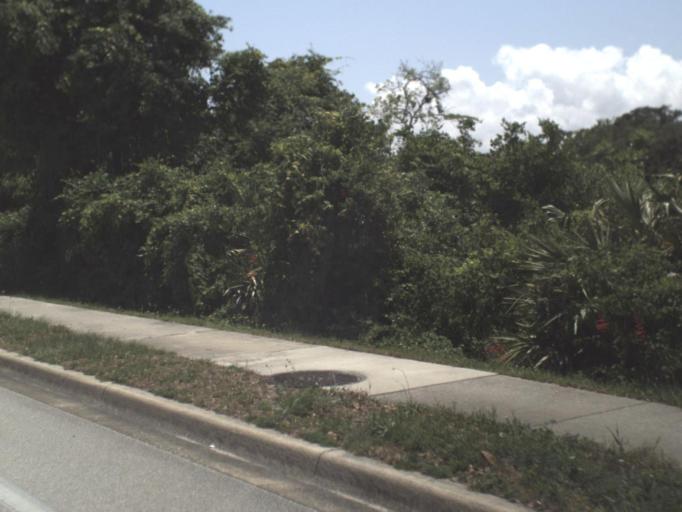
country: US
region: Florida
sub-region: Saint Johns County
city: Saint Augustine Beach
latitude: 29.8394
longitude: -81.2760
